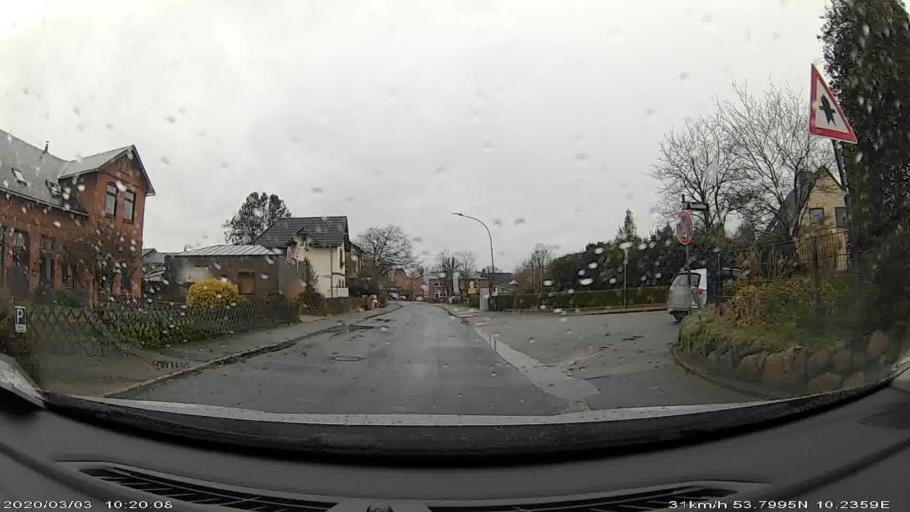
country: DE
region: Schleswig-Holstein
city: Sulfeld
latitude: 53.8002
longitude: 10.2333
